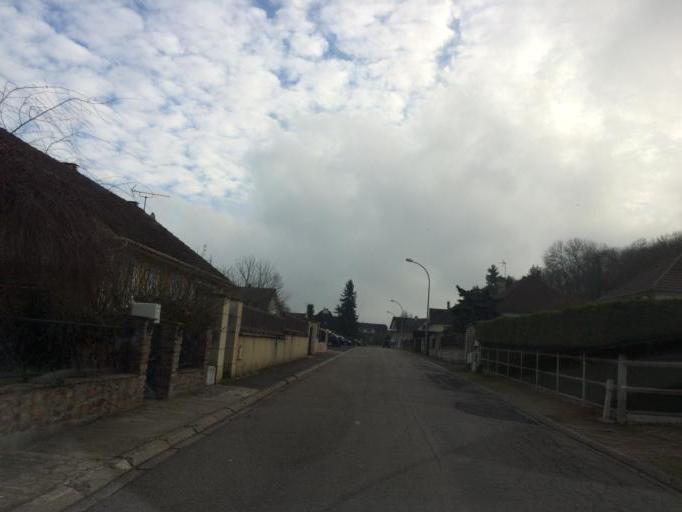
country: FR
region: Ile-de-France
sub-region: Departement de l'Essonne
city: Etrechy
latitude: 48.4849
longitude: 2.1827
